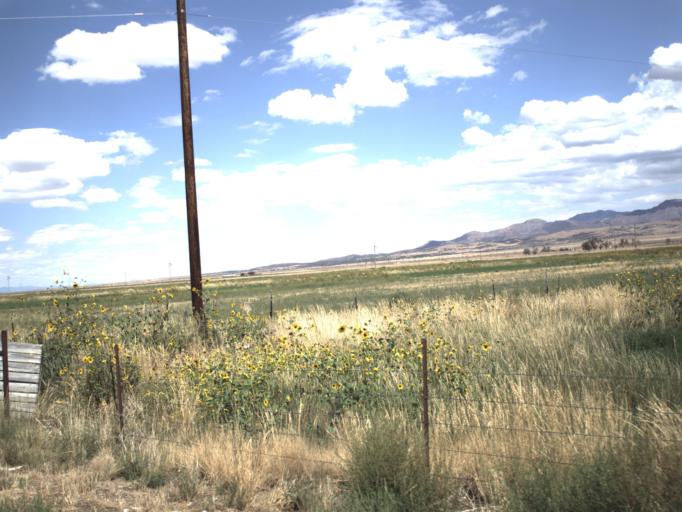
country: US
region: Utah
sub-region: Millard County
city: Delta
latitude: 39.2120
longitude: -112.4152
